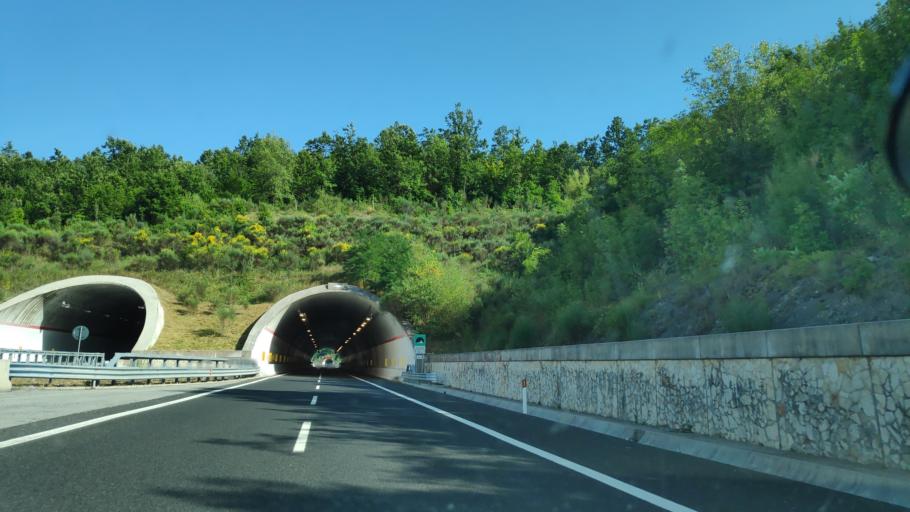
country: IT
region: Campania
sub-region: Provincia di Salerno
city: Casalbuono
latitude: 40.2338
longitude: 15.6641
